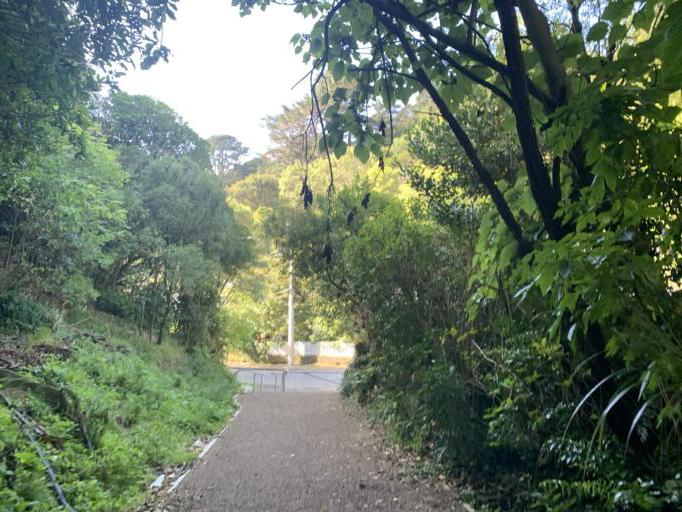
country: NZ
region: Wellington
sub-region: Wellington City
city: Kelburn
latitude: -41.2964
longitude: 174.7566
